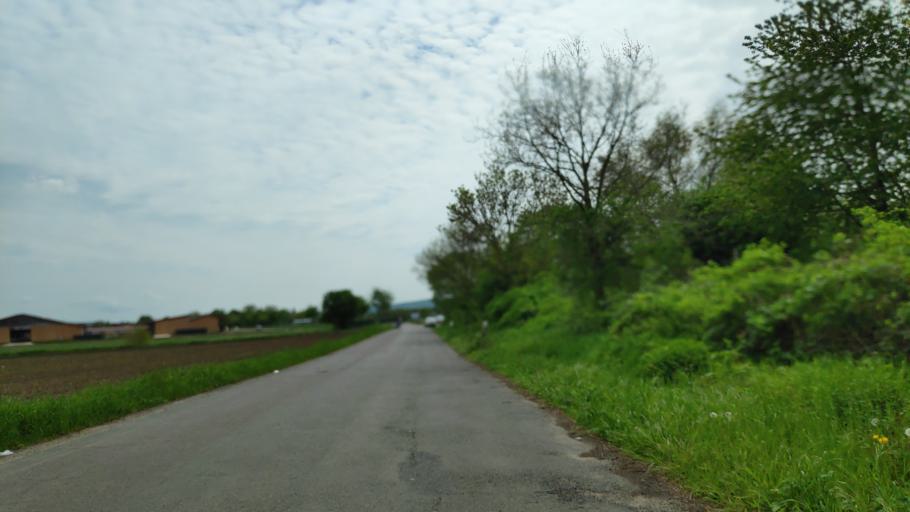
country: DE
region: North Rhine-Westphalia
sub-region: Regierungsbezirk Detmold
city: Minden
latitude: 52.2849
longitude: 8.9818
